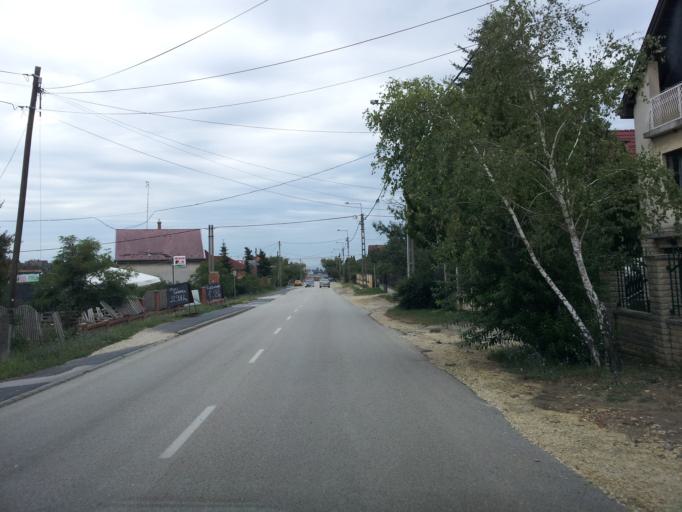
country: HU
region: Pest
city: Toeroekbalint
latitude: 47.4185
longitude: 18.8773
